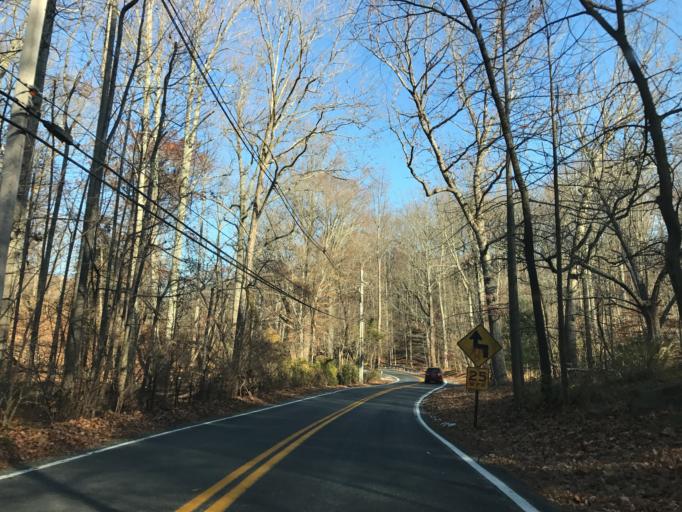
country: US
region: Maryland
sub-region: Howard County
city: Ellicott City
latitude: 39.2538
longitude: -76.7977
